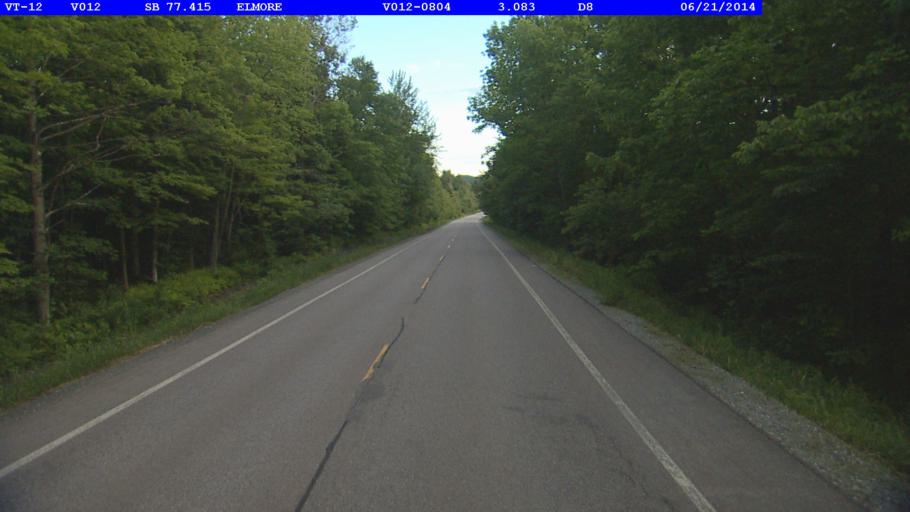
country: US
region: Vermont
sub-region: Lamoille County
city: Morrisville
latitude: 44.4905
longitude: -72.5223
